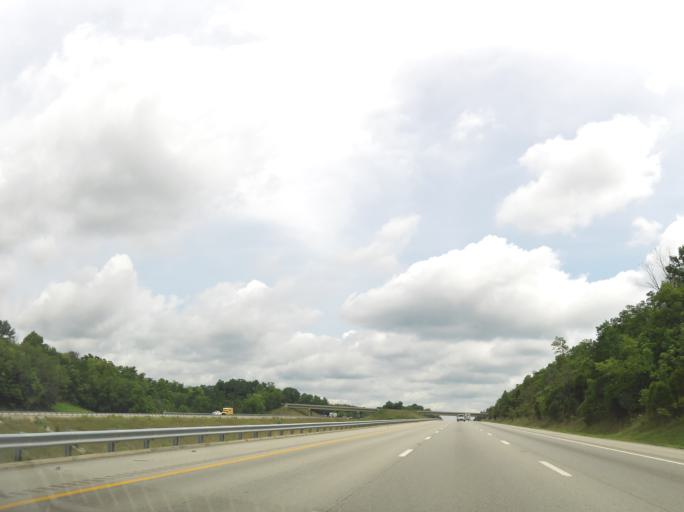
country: US
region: Kentucky
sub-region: Grant County
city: Williamstown
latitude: 38.4284
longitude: -84.5744
